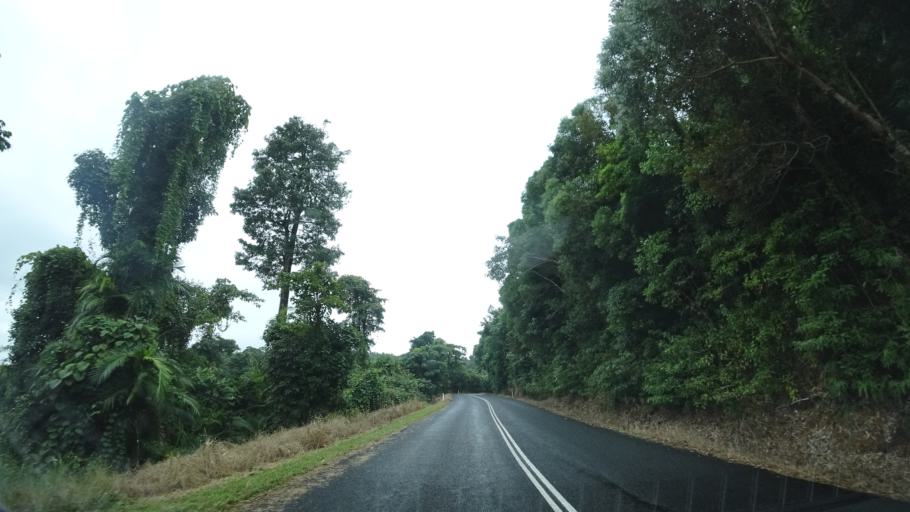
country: AU
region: Queensland
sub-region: Cassowary Coast
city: Innisfail
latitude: -17.5582
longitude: 146.0863
